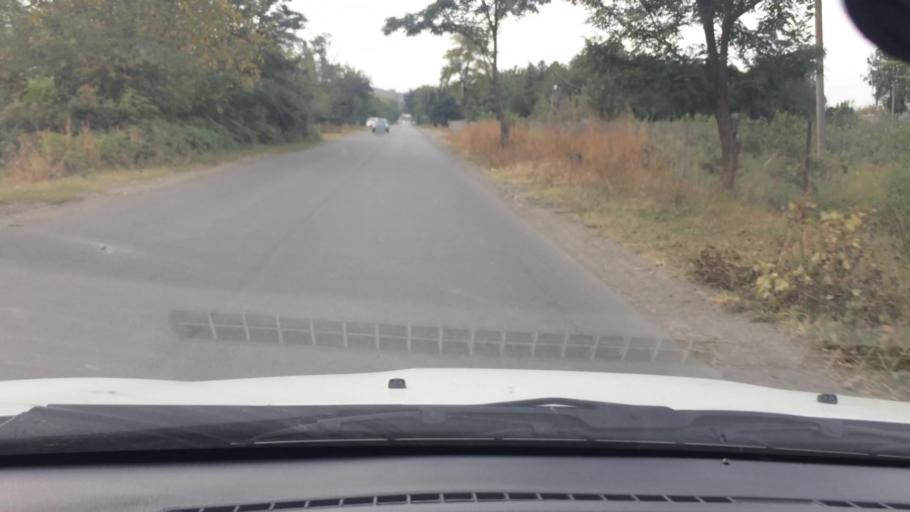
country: GE
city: Naghvarevi
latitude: 41.3569
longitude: 44.8543
